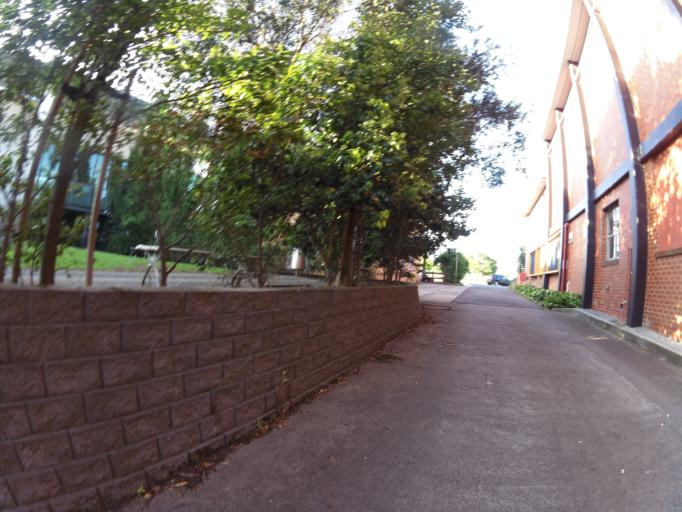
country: AU
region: Victoria
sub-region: Latrobe
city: Morwell
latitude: -38.2369
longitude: 146.3940
